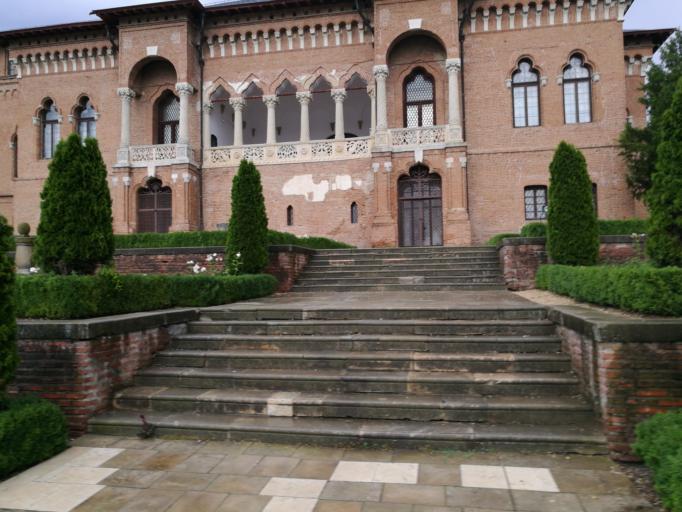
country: RO
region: Ilfov
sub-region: Comuna Mogosoaia
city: Mogosoaia
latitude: 44.5275
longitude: 25.9922
